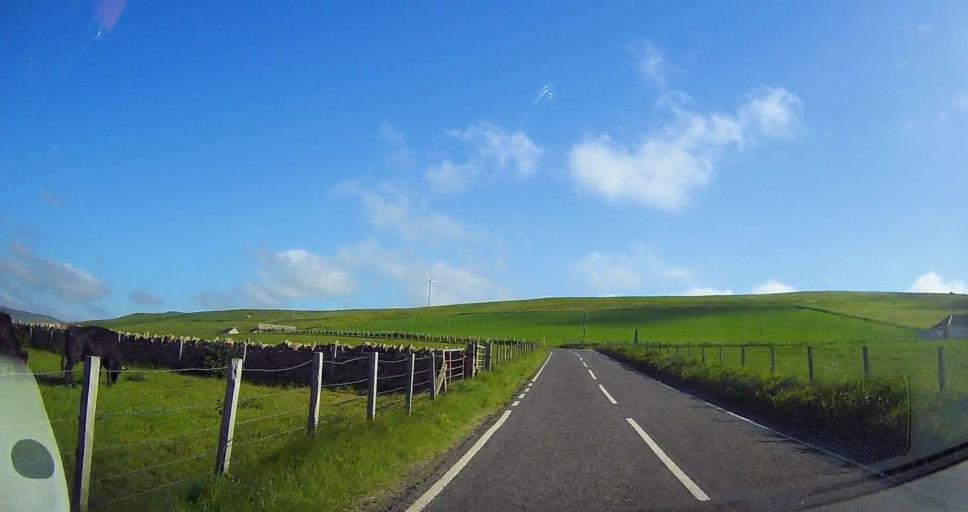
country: GB
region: Scotland
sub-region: Orkney Islands
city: Stromness
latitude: 59.1184
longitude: -3.3070
